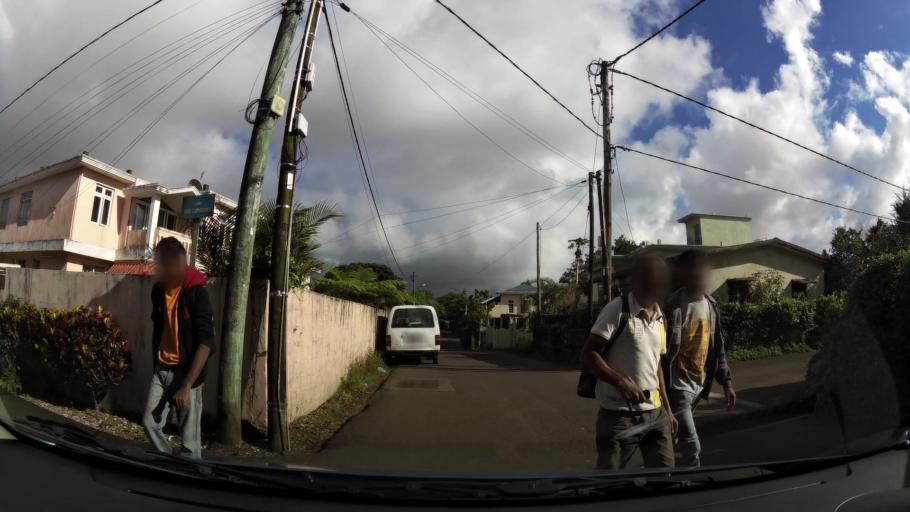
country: MU
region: Plaines Wilhems
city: Curepipe
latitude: -20.3247
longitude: 57.5189
